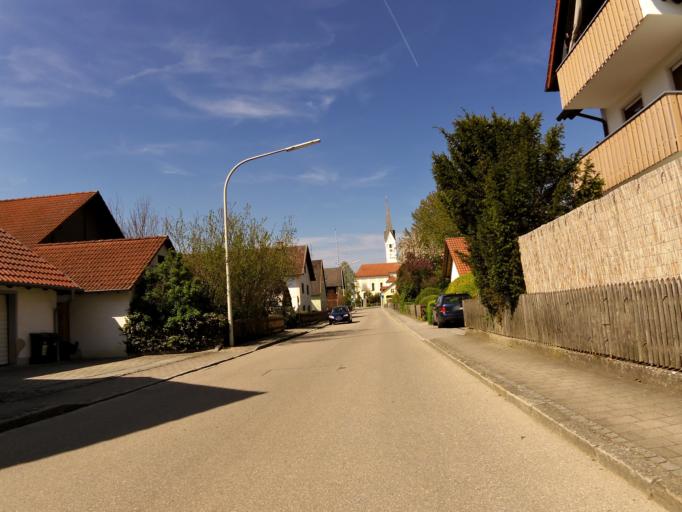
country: DE
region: Bavaria
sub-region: Upper Bavaria
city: Fraunberg
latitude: 48.3668
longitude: 11.9929
